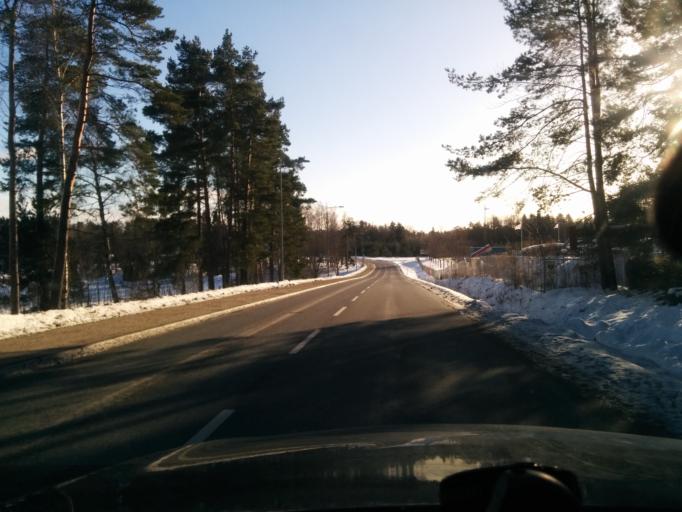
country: SE
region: Stockholm
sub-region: Taby Kommun
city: Taby
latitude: 59.4792
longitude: 18.0941
